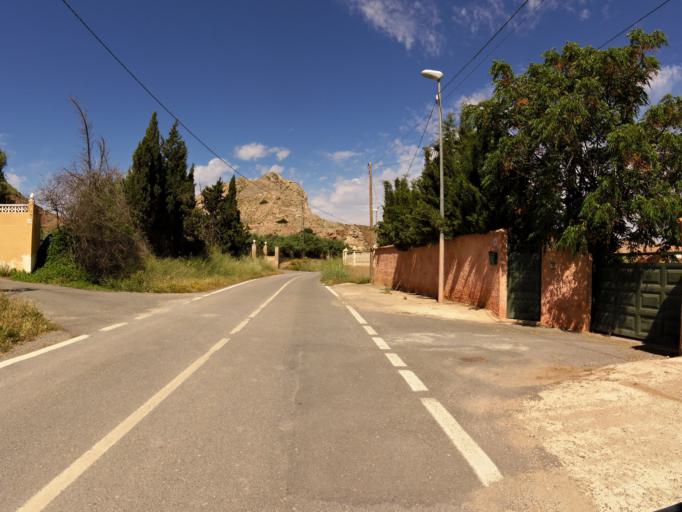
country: ES
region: Valencia
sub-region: Provincia de Alicante
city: Agost
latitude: 38.3956
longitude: -0.6071
